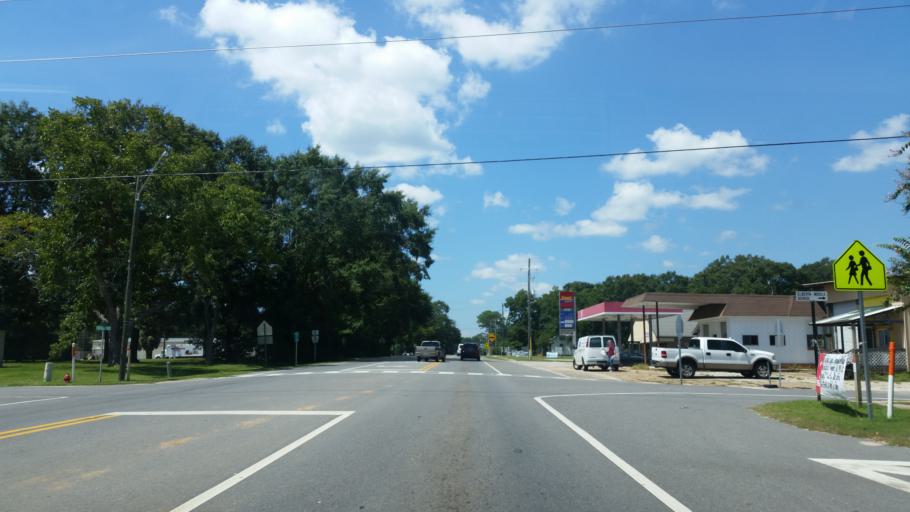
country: US
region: Alabama
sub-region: Baldwin County
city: Elberta
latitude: 30.4144
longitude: -87.5995
